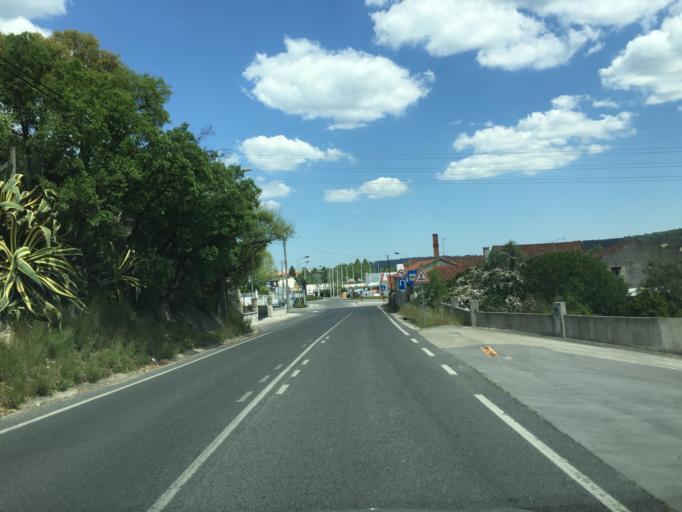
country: PT
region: Santarem
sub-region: Ourem
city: Ourem
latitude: 39.6542
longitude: -8.5934
